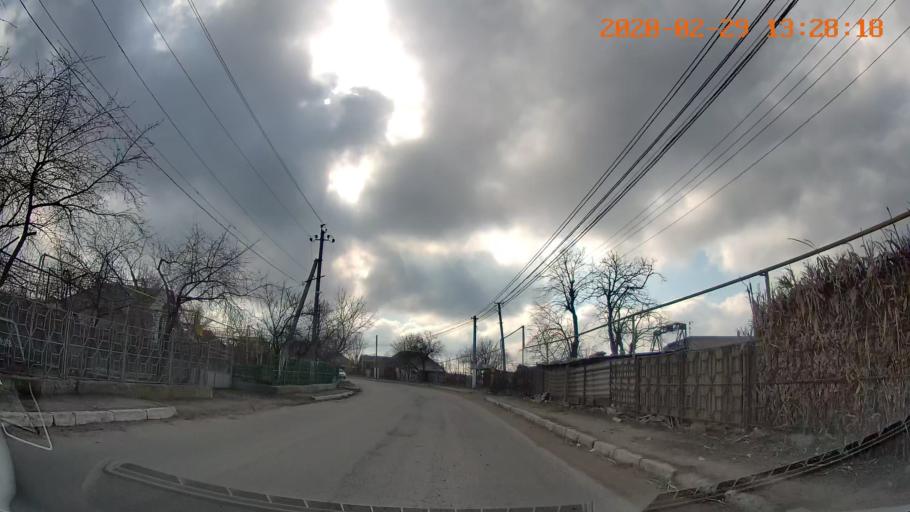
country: MD
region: Telenesti
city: Camenca
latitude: 47.9065
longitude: 28.6427
